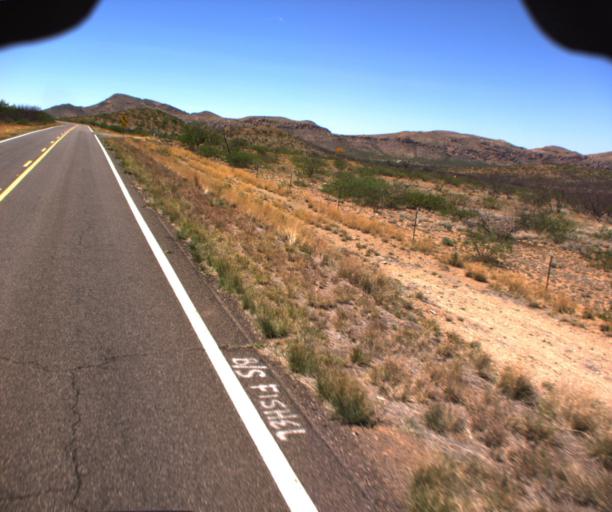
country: US
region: Arizona
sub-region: Cochise County
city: Douglas
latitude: 31.4875
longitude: -109.4369
